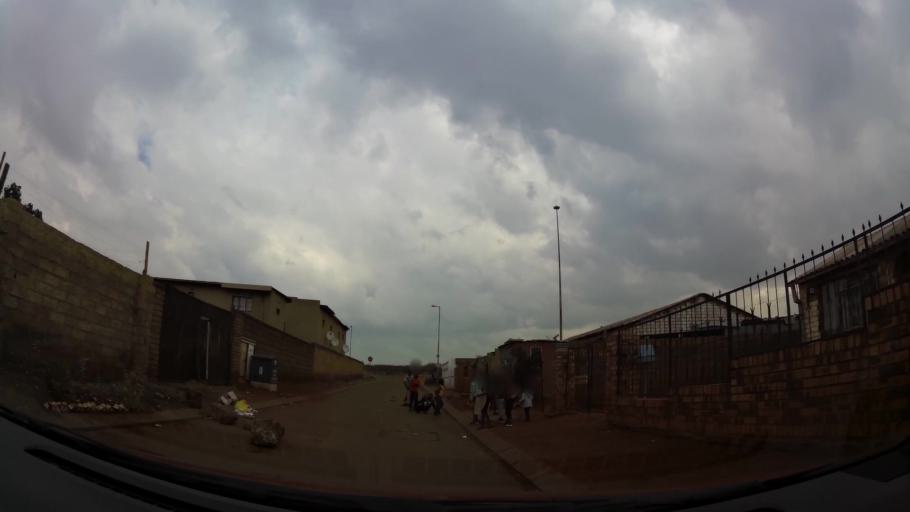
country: ZA
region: Gauteng
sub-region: City of Johannesburg Metropolitan Municipality
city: Soweto
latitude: -26.2584
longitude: 27.8290
